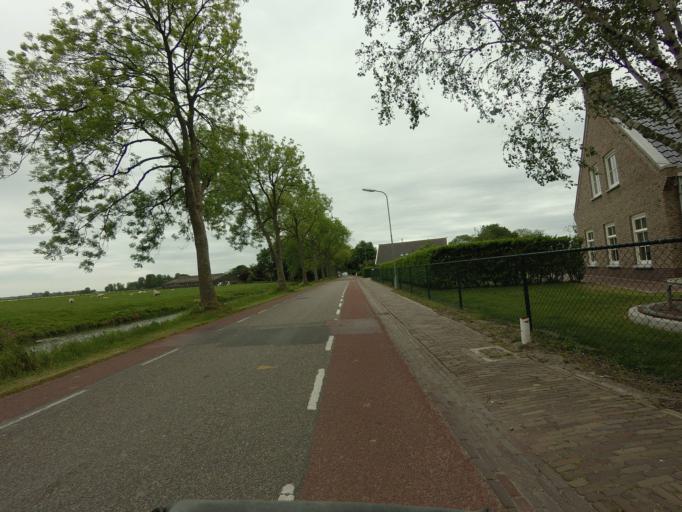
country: NL
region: North Holland
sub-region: Gemeente Medemblik
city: Opperdoes
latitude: 52.7509
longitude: 5.0749
